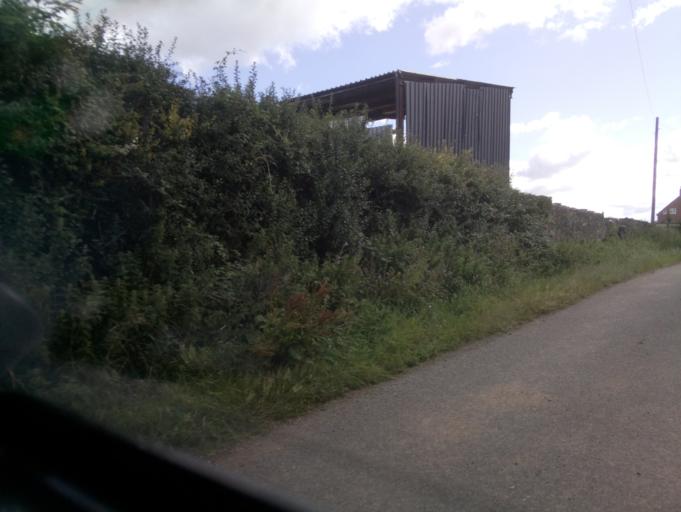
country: GB
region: England
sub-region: Gloucestershire
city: Newent
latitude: 51.8506
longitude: -2.3740
